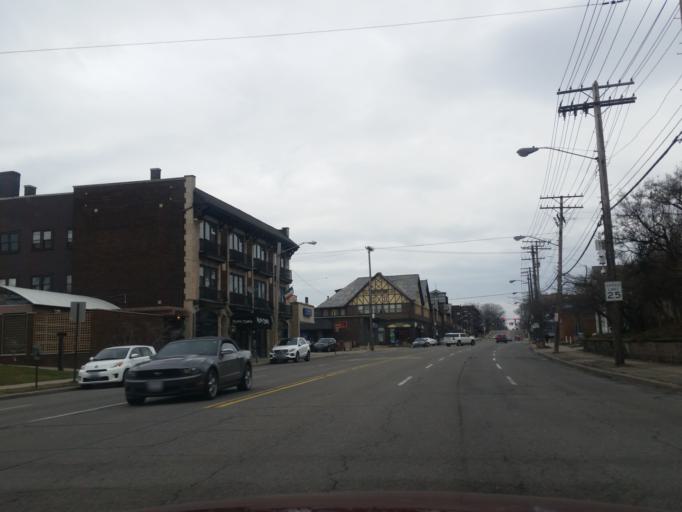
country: US
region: Ohio
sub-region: Cuyahoga County
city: East Cleveland
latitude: 41.5010
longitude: -81.5959
